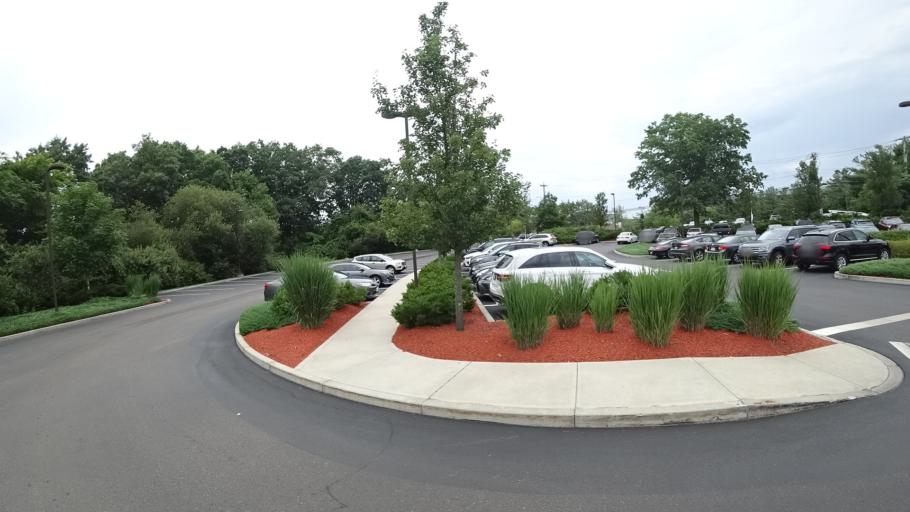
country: US
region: Massachusetts
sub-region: Norfolk County
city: Dedham
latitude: 42.2254
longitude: -71.1721
